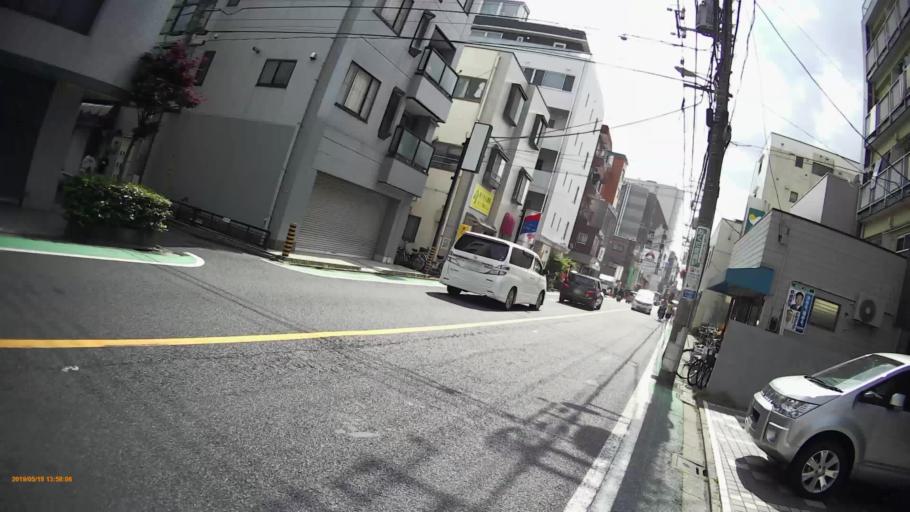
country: JP
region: Tokyo
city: Mitaka-shi
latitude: 35.6700
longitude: 139.6023
